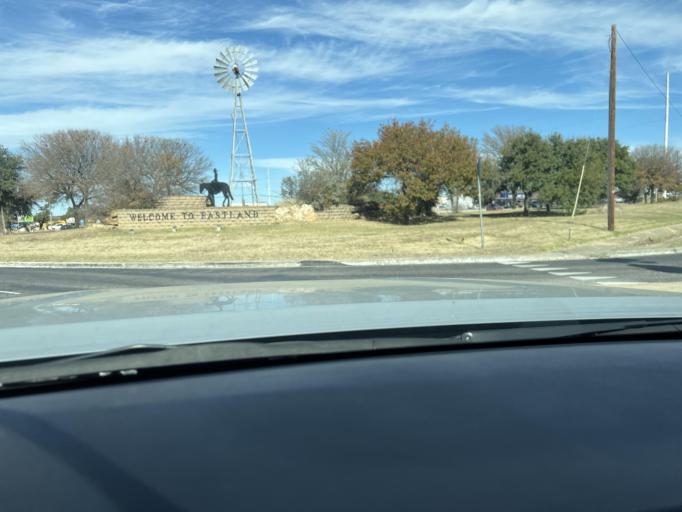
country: US
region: Texas
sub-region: Eastland County
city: Eastland
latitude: 32.4010
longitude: -98.7902
